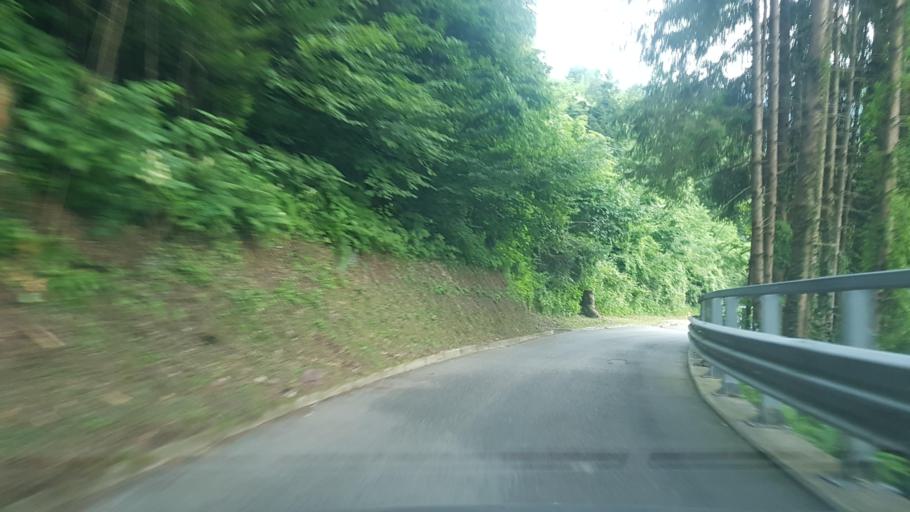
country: IT
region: Friuli Venezia Giulia
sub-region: Provincia di Udine
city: Paularo
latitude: 46.5384
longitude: 13.1214
